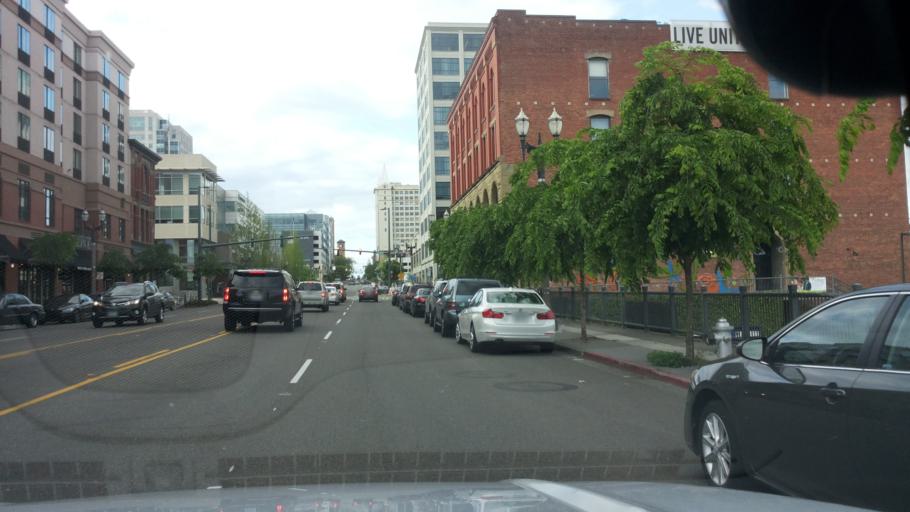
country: US
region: Washington
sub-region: Pierce County
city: Tacoma
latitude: 47.2484
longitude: -122.4374
